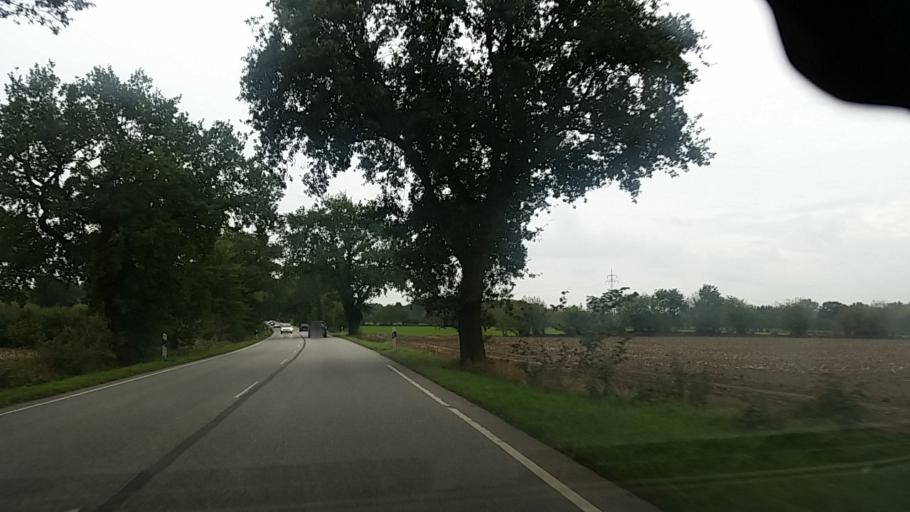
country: DE
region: Schleswig-Holstein
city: Kayhude
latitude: 53.7781
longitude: 10.1261
